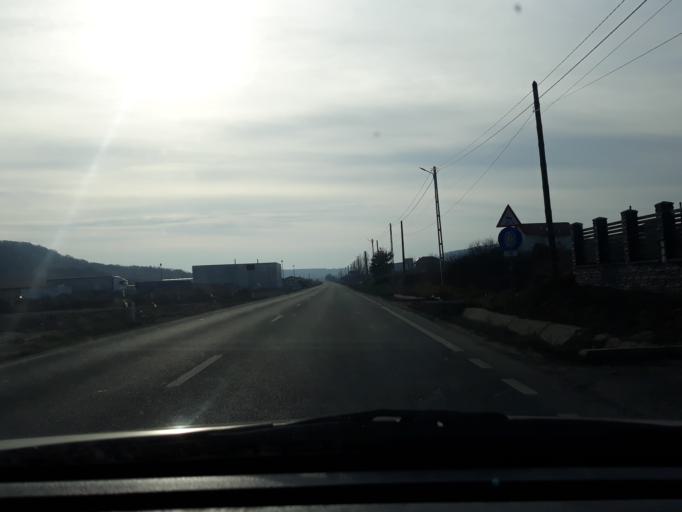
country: RO
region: Salaj
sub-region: Comuna Hereclean
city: Hereclean
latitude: 47.2369
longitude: 22.9854
